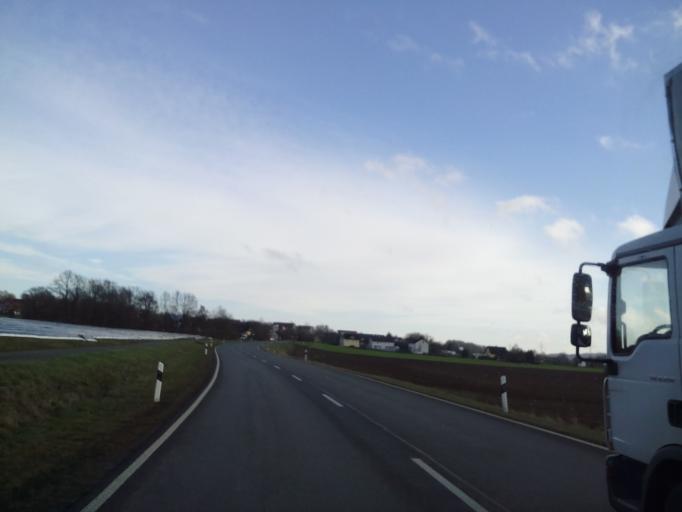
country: DE
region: Bavaria
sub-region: Upper Franconia
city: Mainleus
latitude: 50.1188
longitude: 11.3315
